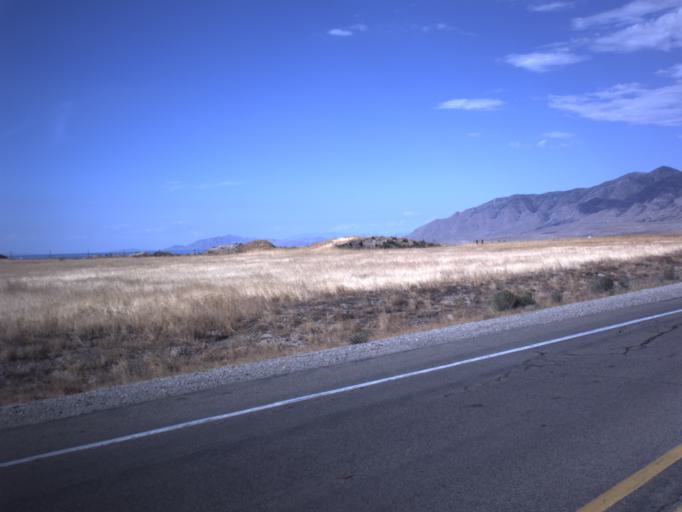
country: US
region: Utah
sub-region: Tooele County
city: Tooele
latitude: 40.5503
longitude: -112.3379
